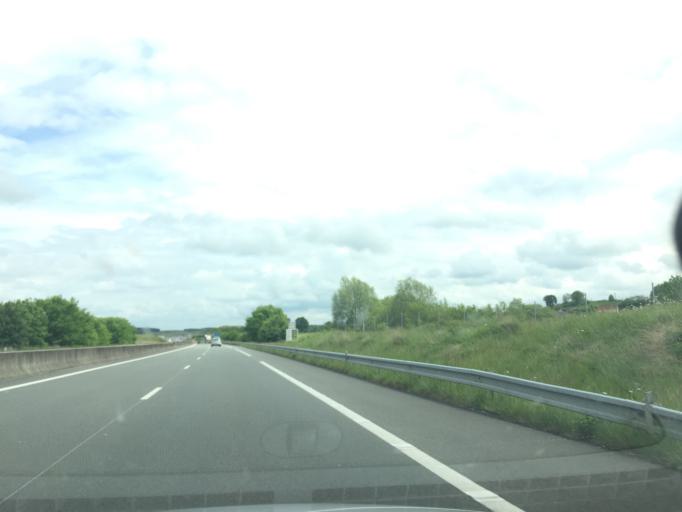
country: FR
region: Centre
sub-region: Departement d'Indre-et-Loire
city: Saint-Christophe-sur-le-Nais
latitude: 47.6523
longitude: 0.4521
